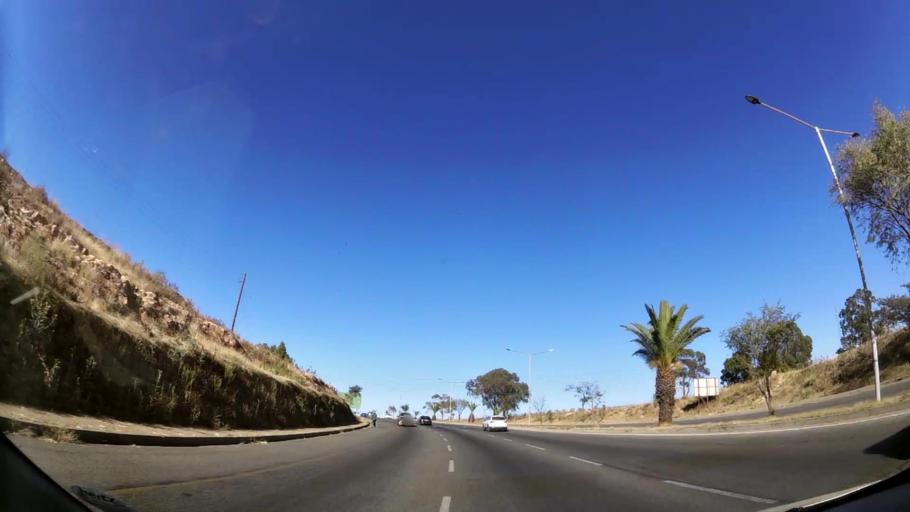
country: ZA
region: Gauteng
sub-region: West Rand District Municipality
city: Krugersdorp
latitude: -26.1115
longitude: 27.7760
